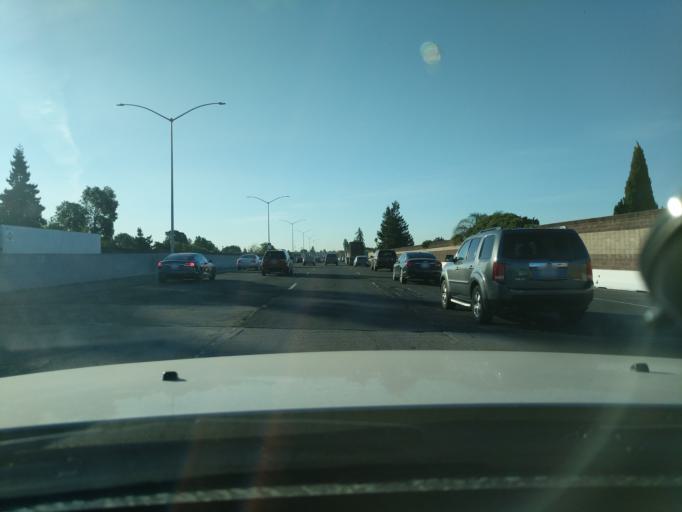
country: US
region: California
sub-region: Alameda County
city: Union City
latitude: 37.5956
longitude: -122.0588
